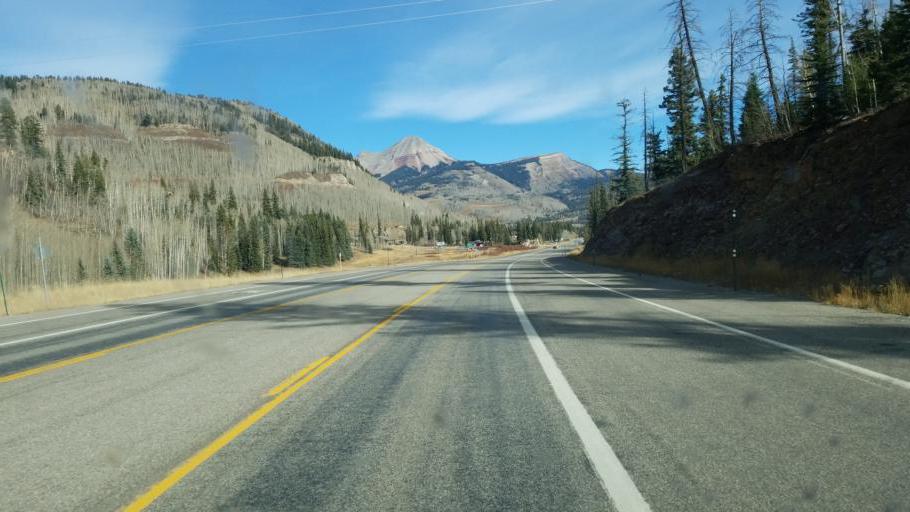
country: US
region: Colorado
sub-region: San Juan County
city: Silverton
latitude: 37.6218
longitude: -107.8117
